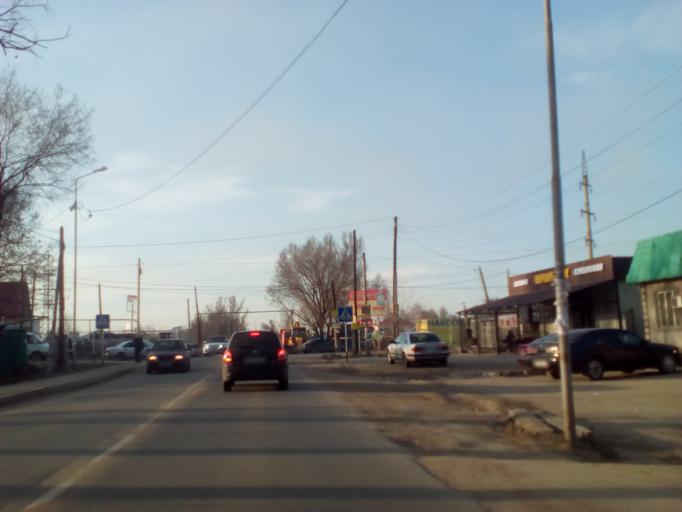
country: KZ
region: Almaty Oblysy
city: Burunday
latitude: 43.2593
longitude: 76.7794
